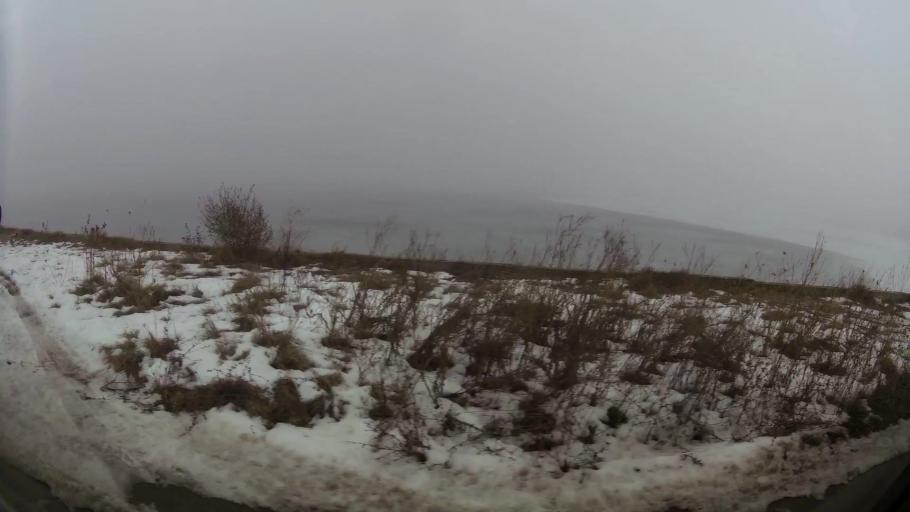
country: RO
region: Ilfov
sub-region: Comuna Chiajna
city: Rosu
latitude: 44.4504
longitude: 26.0279
